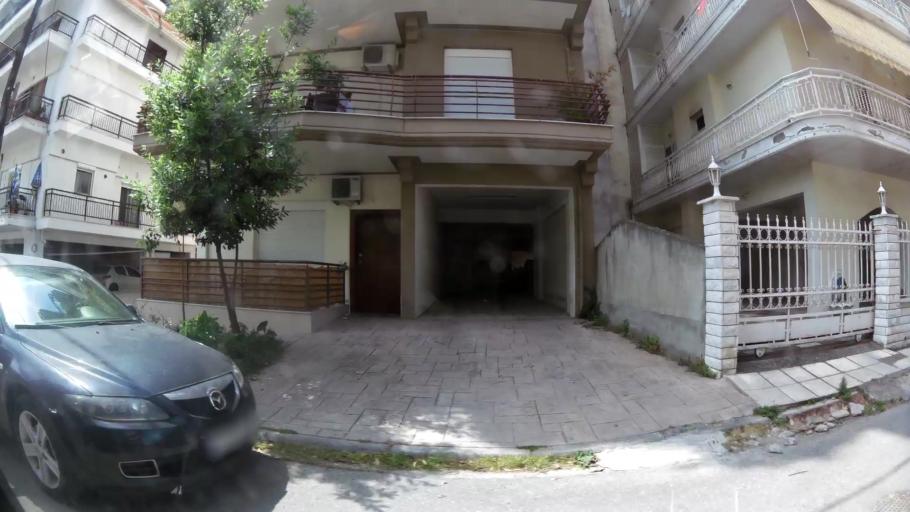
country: GR
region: Central Macedonia
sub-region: Nomos Pierias
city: Katerini
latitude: 40.2728
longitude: 22.4990
